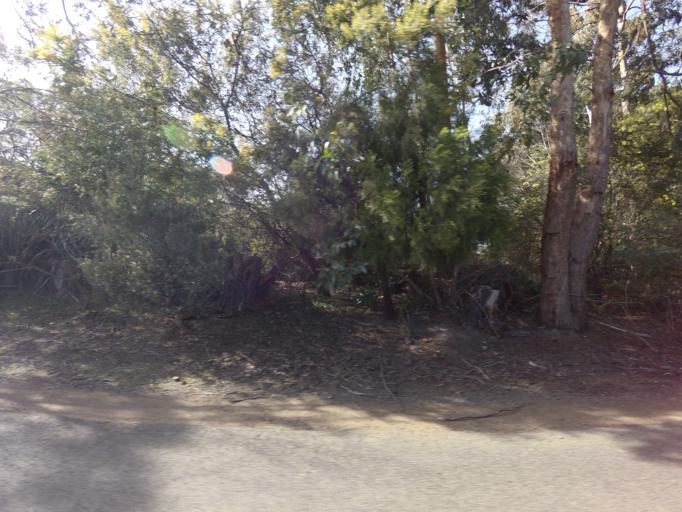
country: AU
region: Tasmania
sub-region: Kingborough
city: Kettering
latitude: -43.1099
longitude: 147.2567
